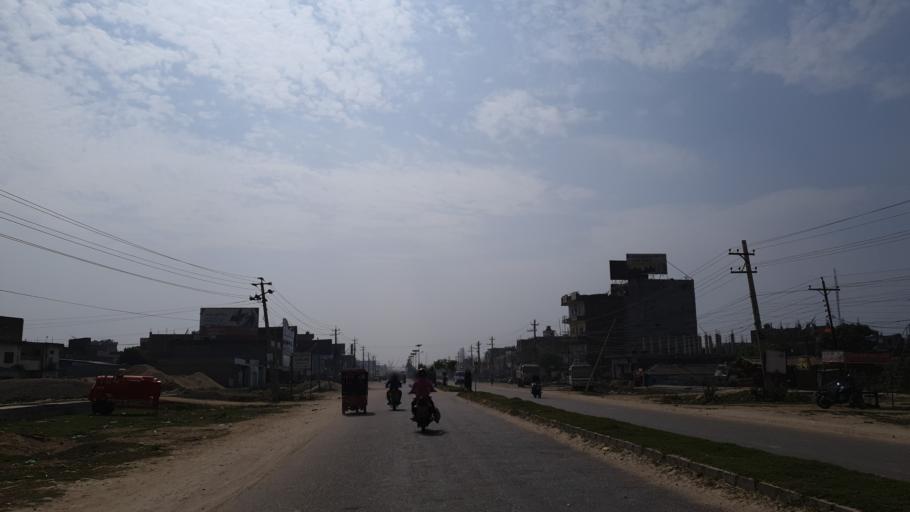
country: NP
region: Central Region
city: Janakpur
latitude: 26.7461
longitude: 85.9229
